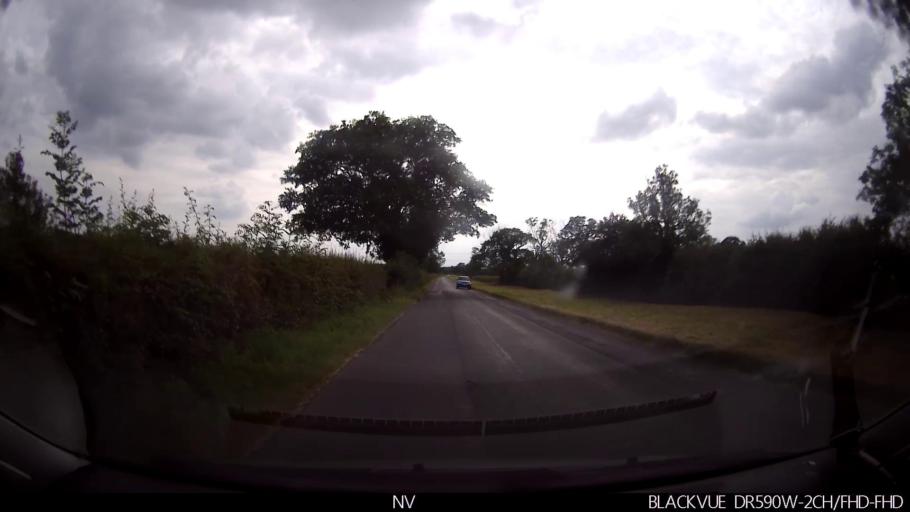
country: GB
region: England
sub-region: North Yorkshire
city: Strensall
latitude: 54.0512
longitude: -0.9662
